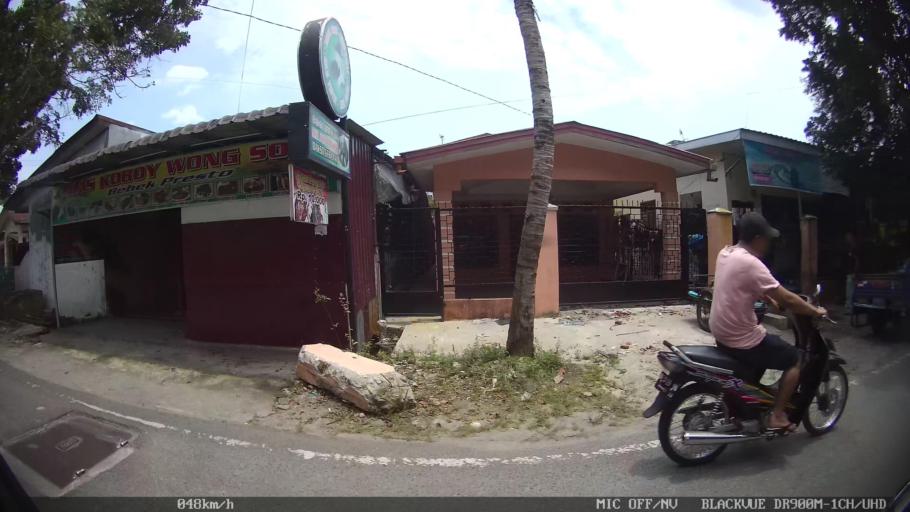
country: ID
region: North Sumatra
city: Medan
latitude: 3.5551
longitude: 98.6551
